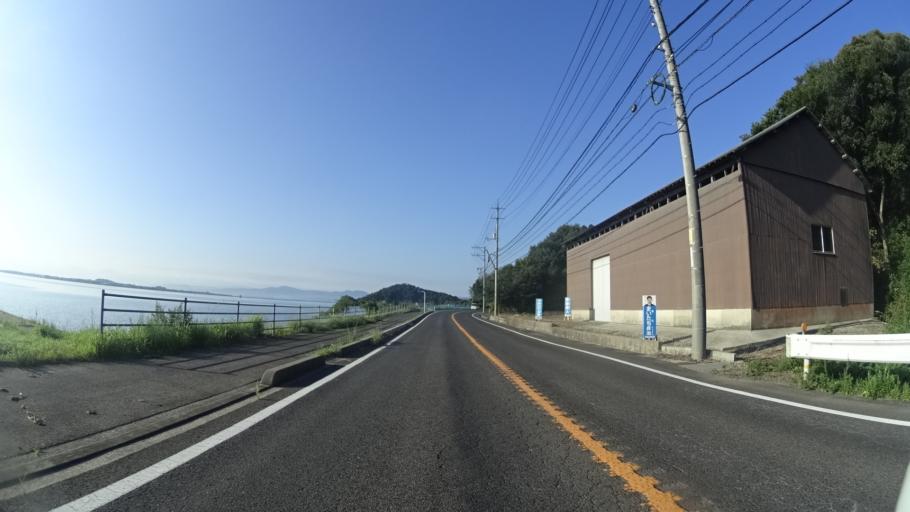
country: JP
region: Shimane
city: Sakaiminato
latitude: 35.5274
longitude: 133.1496
